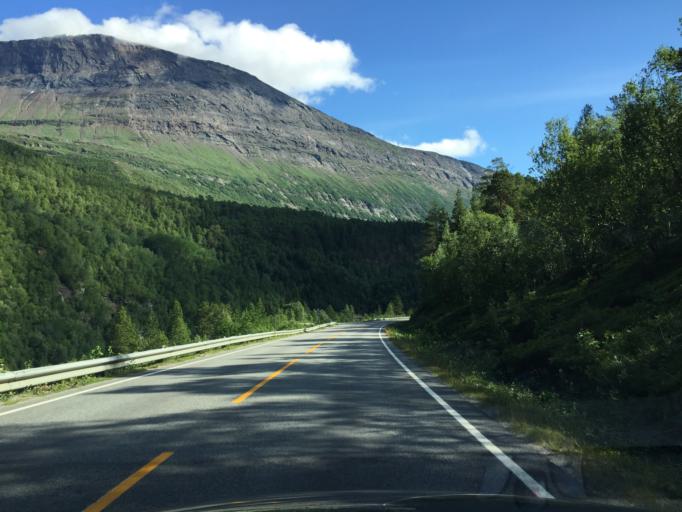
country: NO
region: Nordland
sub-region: Saltdal
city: Rognan
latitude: 66.8241
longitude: 15.4931
